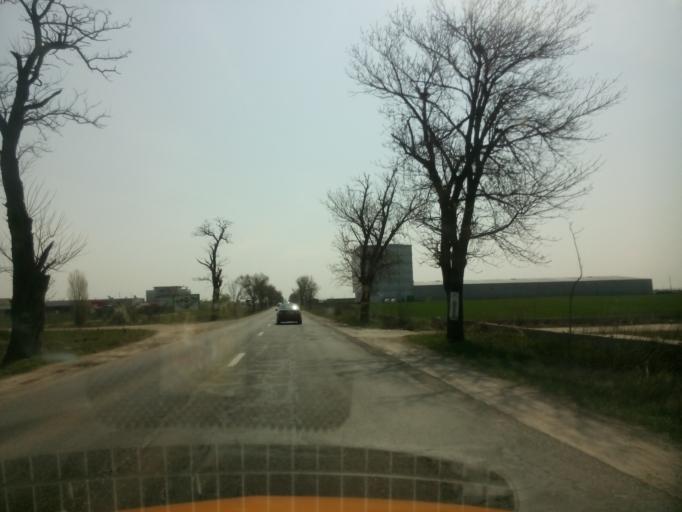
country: RO
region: Ilfov
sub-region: Comuna Glina
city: Glina
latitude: 44.3428
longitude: 26.2304
